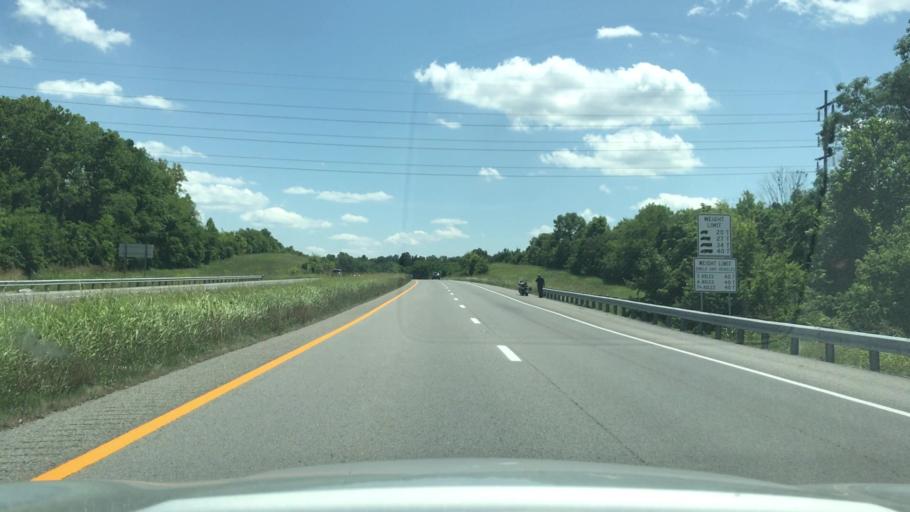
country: US
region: Kentucky
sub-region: Christian County
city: Hopkinsville
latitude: 36.8816
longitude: -87.4688
